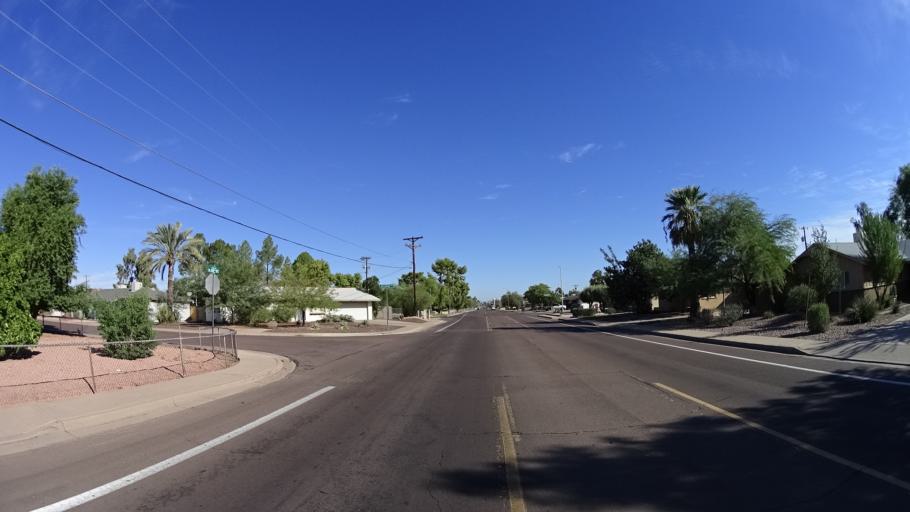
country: US
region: Arizona
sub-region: Maricopa County
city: Scottsdale
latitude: 33.4760
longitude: -111.9348
